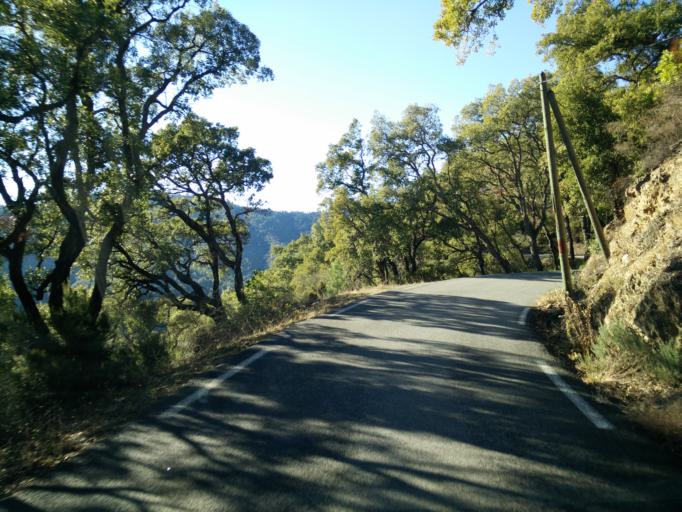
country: FR
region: Provence-Alpes-Cote d'Azur
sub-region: Departement du Var
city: La Garde-Freinet
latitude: 43.2588
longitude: 6.4482
